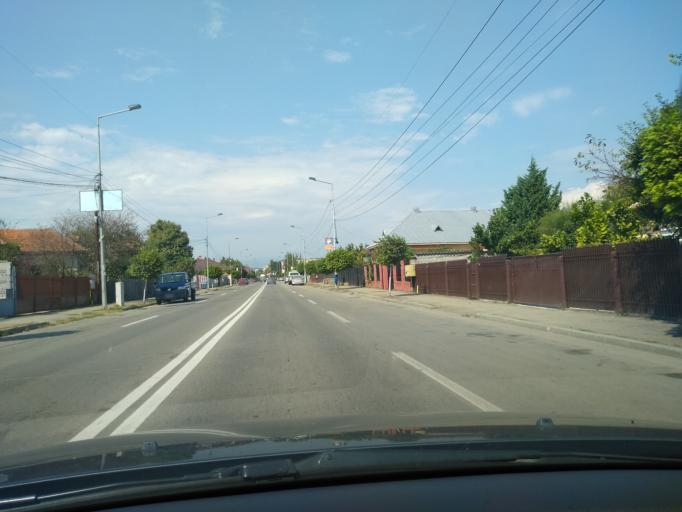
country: RO
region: Gorj
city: Targu Jiu
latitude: 45.0191
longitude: 23.2682
